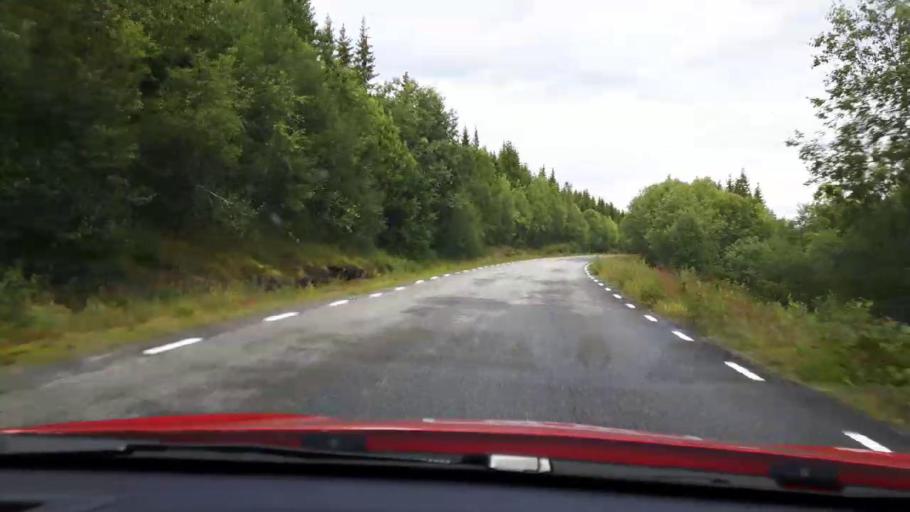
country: SE
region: Jaemtland
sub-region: Are Kommun
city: Are
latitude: 63.7219
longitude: 12.9682
